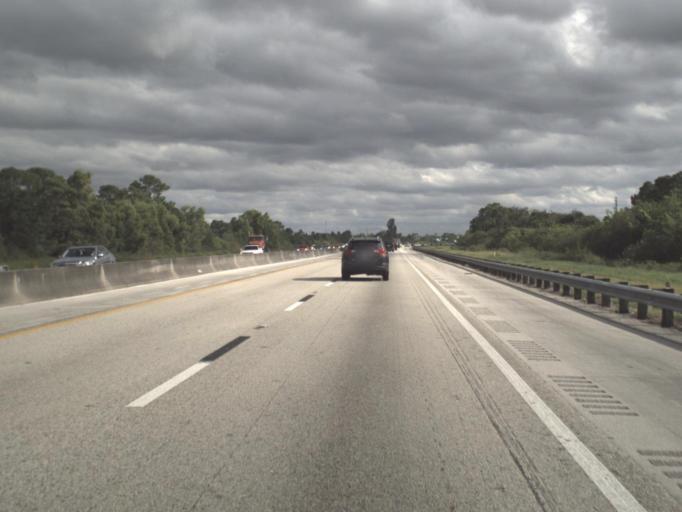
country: US
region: Florida
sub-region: Martin County
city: Palm City
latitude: 27.1034
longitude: -80.2639
